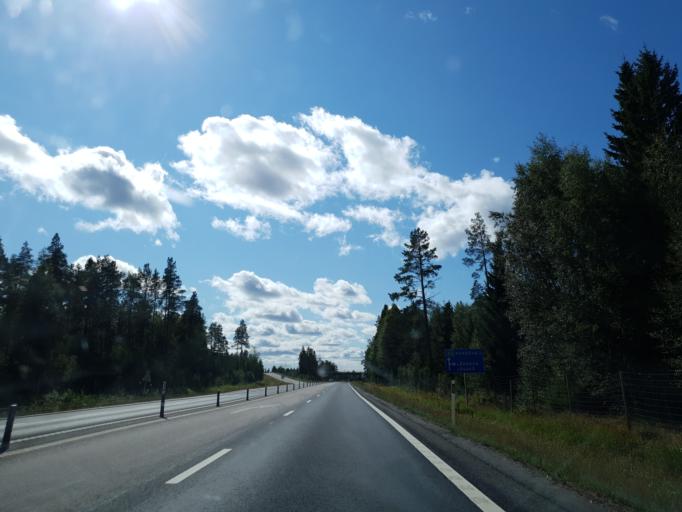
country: SE
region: Vaesterbotten
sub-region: Nordmalings Kommun
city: Nordmaling
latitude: 63.5404
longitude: 19.4055
